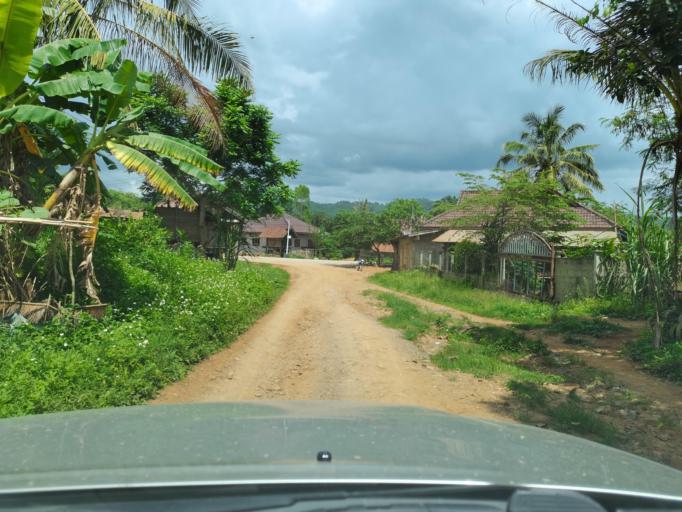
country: LA
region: Loungnamtha
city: Muang Long
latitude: 20.6799
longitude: 101.0570
